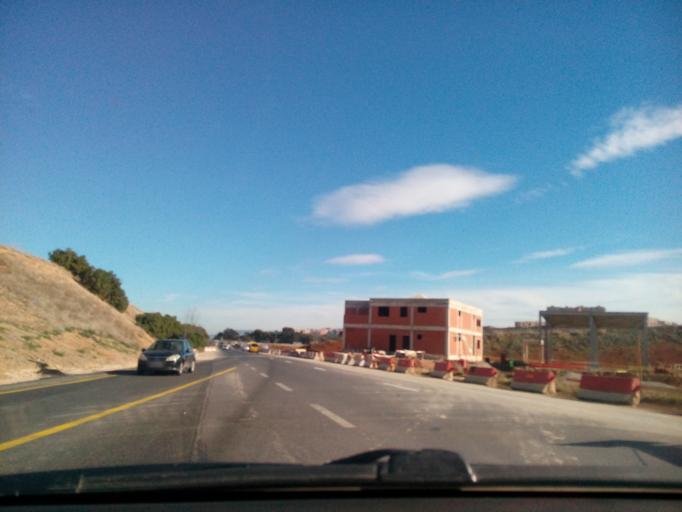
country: DZ
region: Tlemcen
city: Hennaya
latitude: 34.9237
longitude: -1.3646
